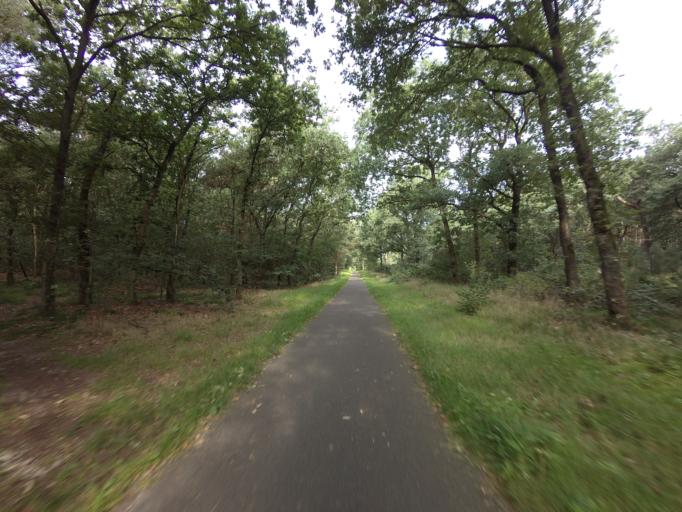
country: DE
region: Lower Saxony
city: Itterbeck
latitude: 52.5084
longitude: 6.7900
